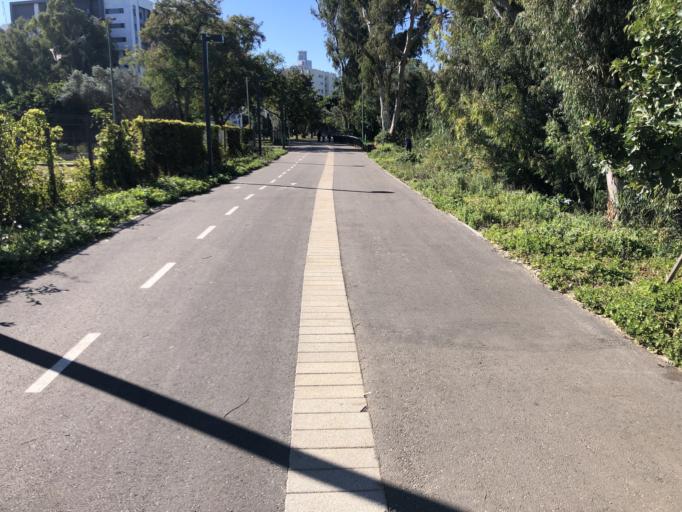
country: IL
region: Tel Aviv
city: Ramat Gan
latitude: 32.0971
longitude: 34.8153
